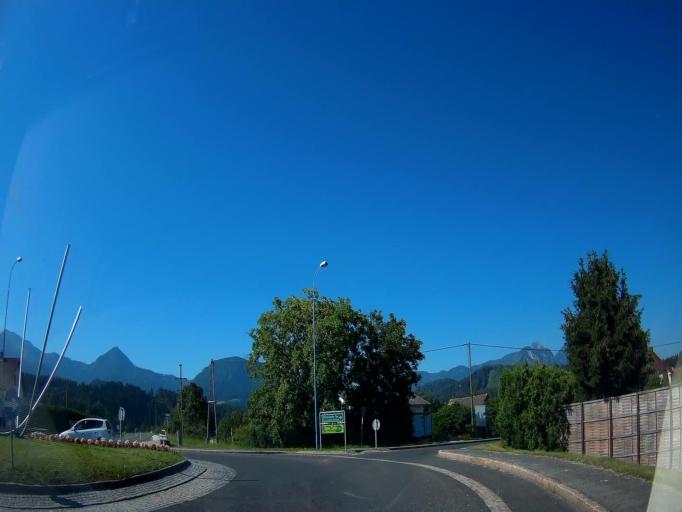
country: AT
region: Carinthia
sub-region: Politischer Bezirk Volkermarkt
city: Eberndorf
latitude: 46.5757
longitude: 14.6284
